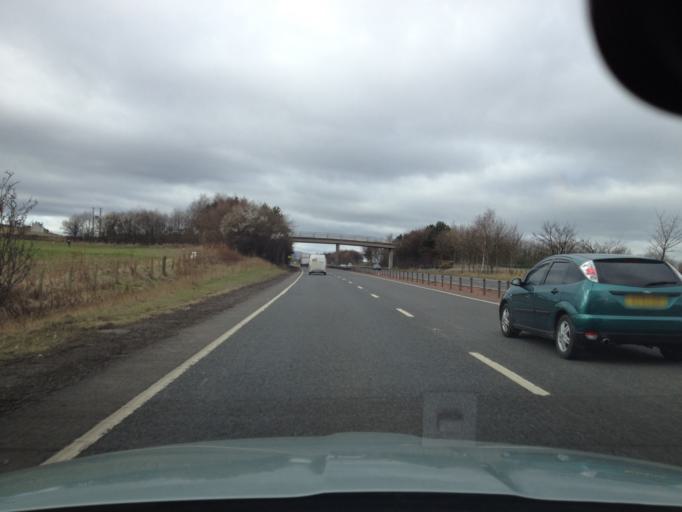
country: GB
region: Scotland
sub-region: East Lothian
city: Prestonpans
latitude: 55.9503
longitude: -2.9687
